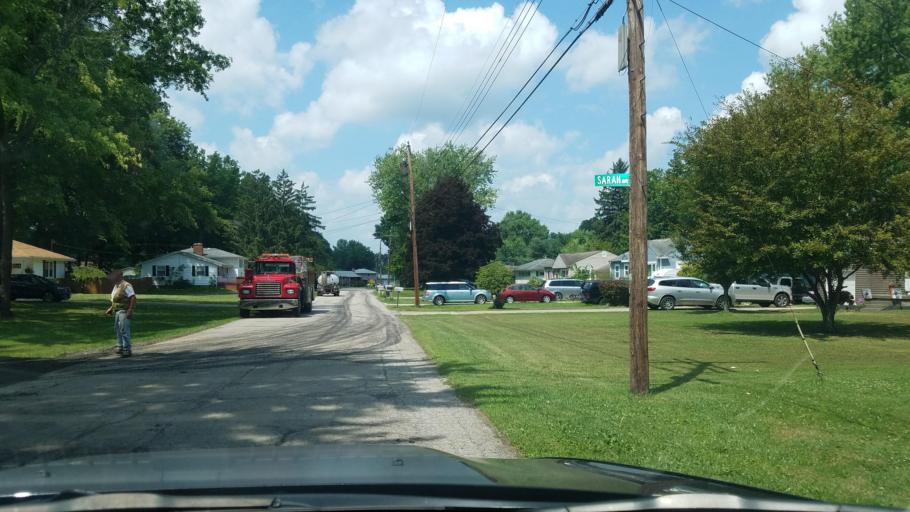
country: US
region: Ohio
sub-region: Trumbull County
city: Champion Heights
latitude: 41.3136
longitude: -80.8559
